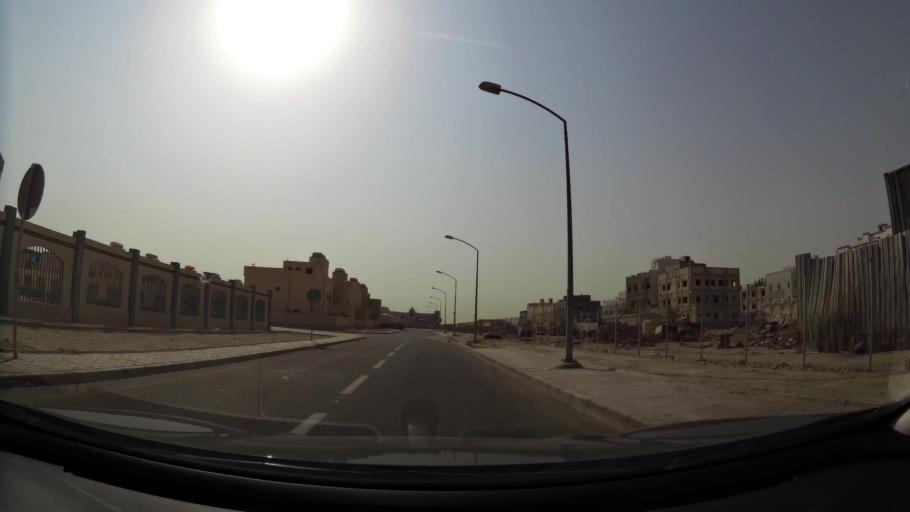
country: KW
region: Muhafazat al Jahra'
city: Al Jahra'
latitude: 29.3493
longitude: 47.7530
